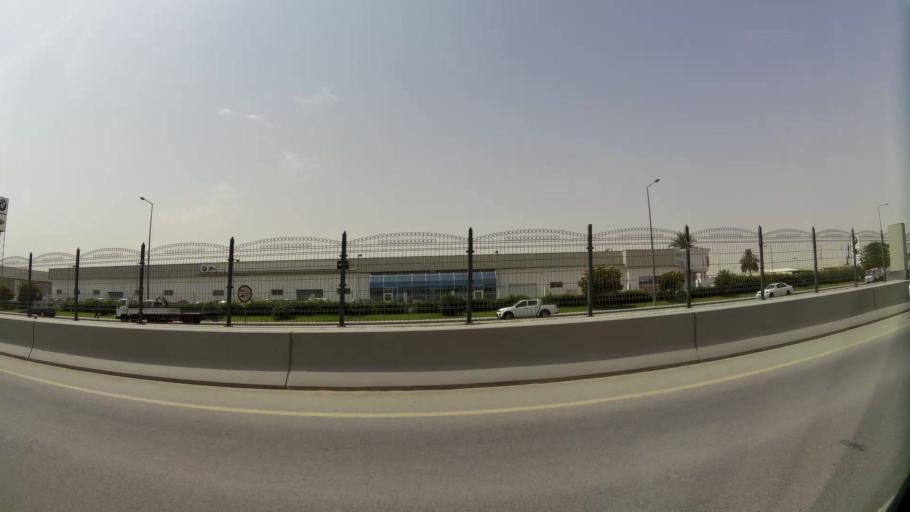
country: QA
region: Baladiyat ar Rayyan
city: Ar Rayyan
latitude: 25.2206
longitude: 51.4353
